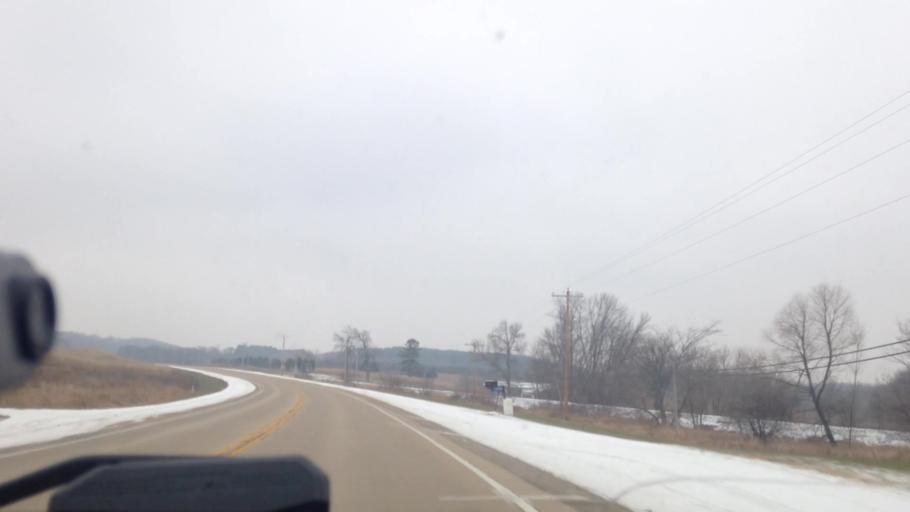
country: US
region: Wisconsin
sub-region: Dodge County
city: Mayville
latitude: 43.4667
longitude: -88.5464
